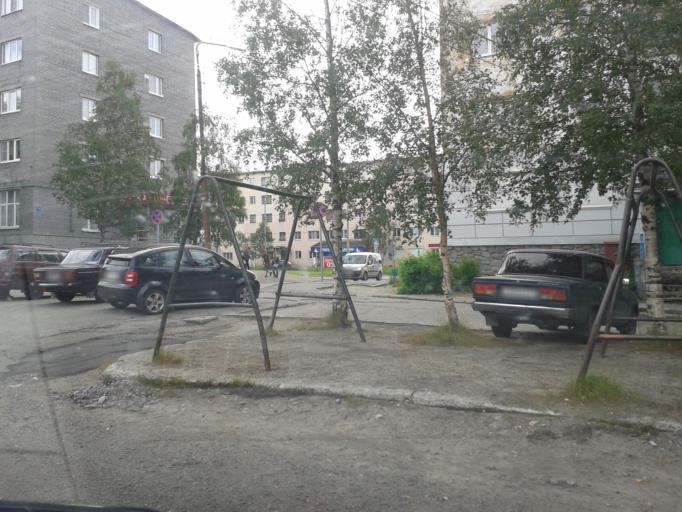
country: RU
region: Murmansk
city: Kandalaksha
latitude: 67.1518
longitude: 32.4090
